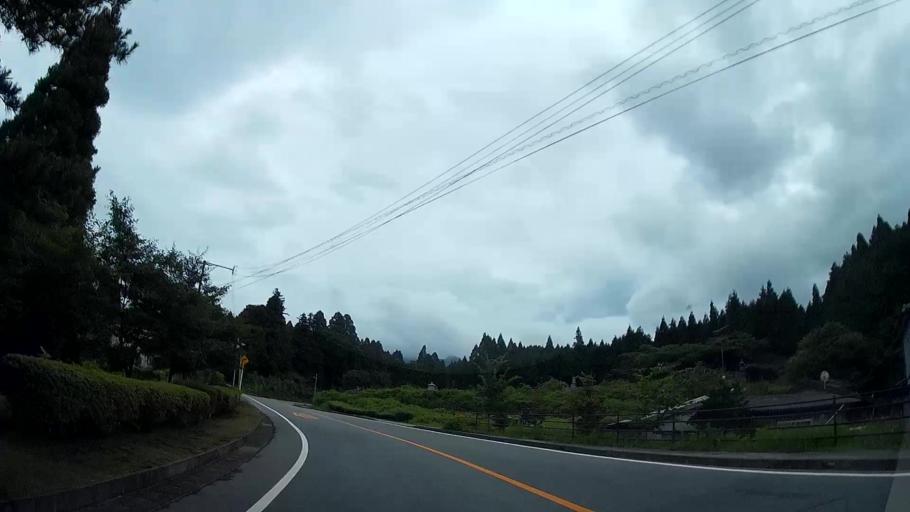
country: JP
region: Kumamoto
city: Aso
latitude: 32.9294
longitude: 131.0788
